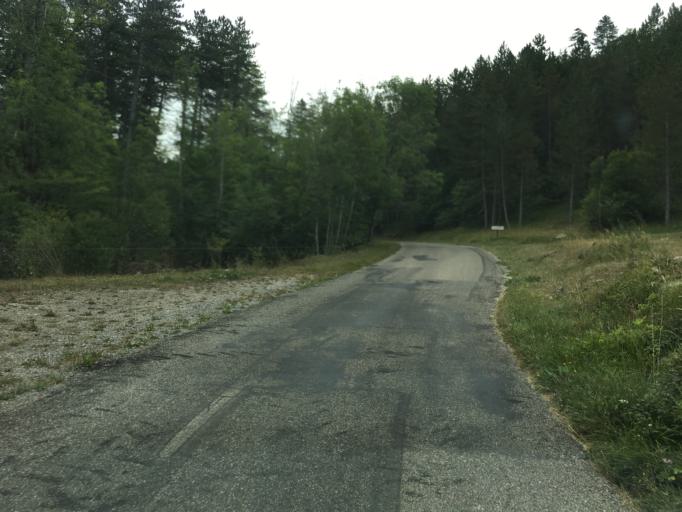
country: FR
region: Provence-Alpes-Cote d'Azur
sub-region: Departement des Alpes-de-Haute-Provence
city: Volonne
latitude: 44.2288
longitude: 6.1325
